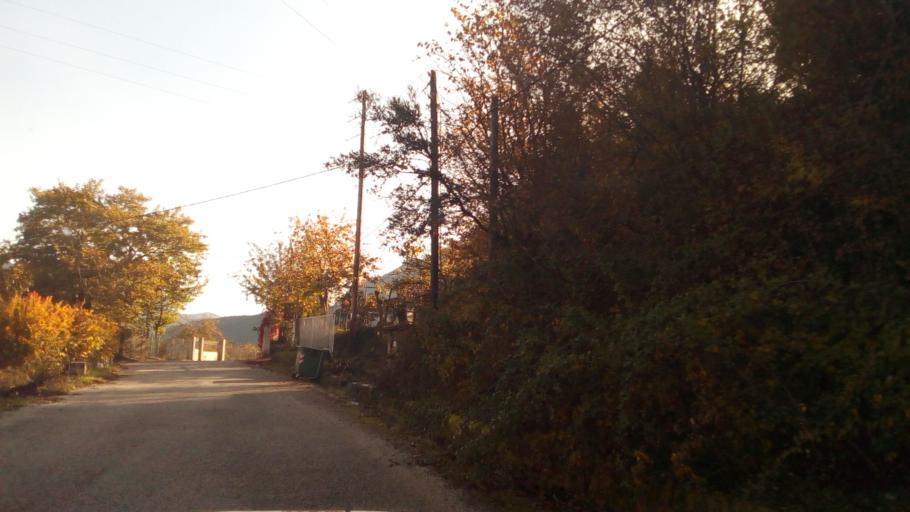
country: GR
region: West Greece
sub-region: Nomos Aitolias kai Akarnanias
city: Thermo
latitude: 38.6548
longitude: 21.8478
